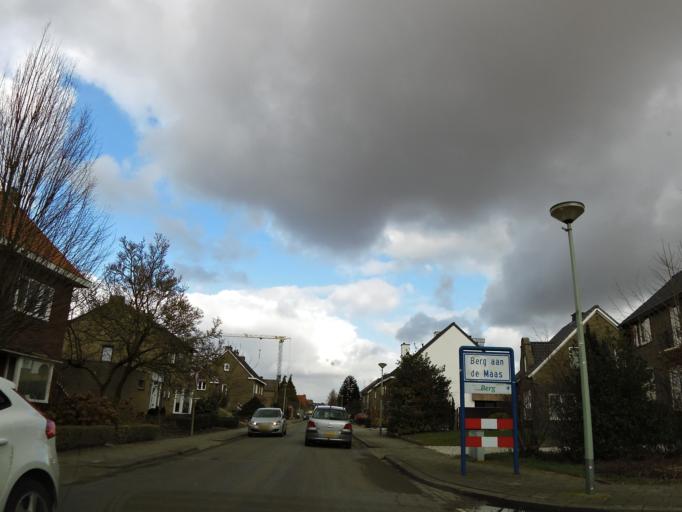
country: NL
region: Limburg
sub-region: Gemeente Stein
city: Urmond
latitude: 50.9973
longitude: 5.7703
